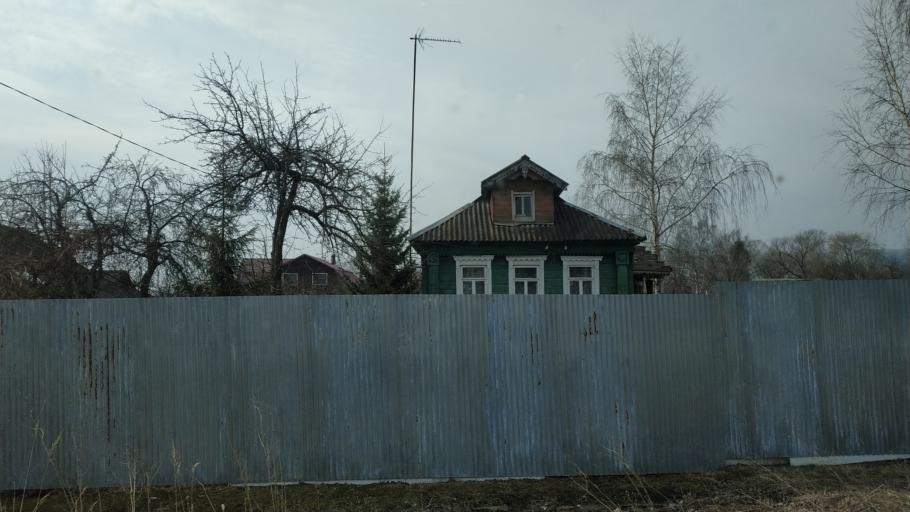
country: RU
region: Moskovskaya
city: Ashitkovo
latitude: 55.4219
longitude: 38.5486
